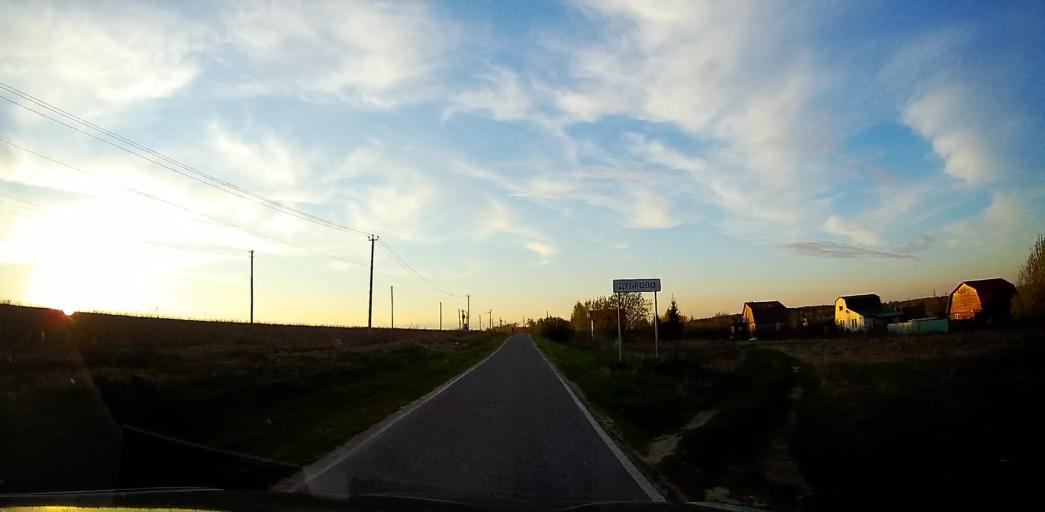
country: RU
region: Moskovskaya
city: Peski
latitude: 55.2256
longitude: 38.7353
